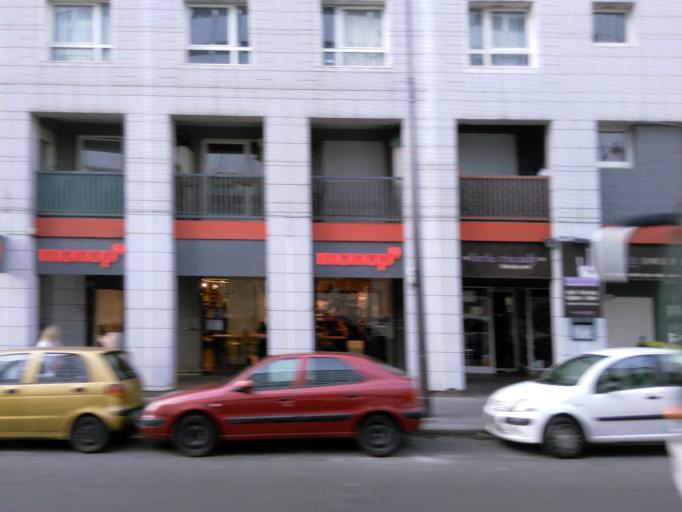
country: FR
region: Ile-de-France
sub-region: Departement des Hauts-de-Seine
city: Issy-les-Moulineaux
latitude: 48.8520
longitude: 2.2774
